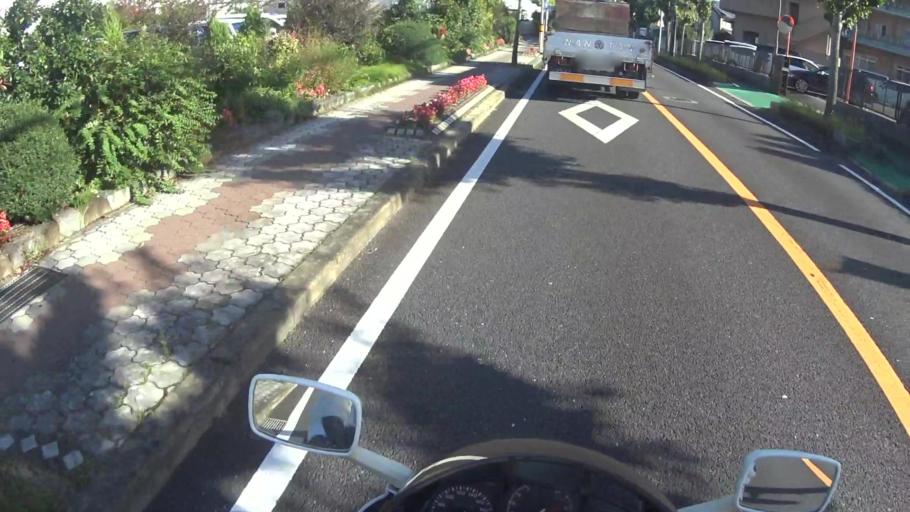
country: JP
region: Kyoto
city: Kameoka
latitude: 35.0108
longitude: 135.5875
